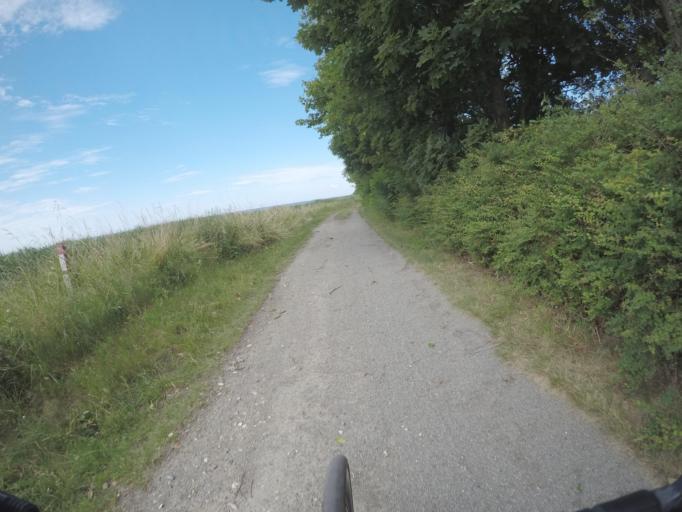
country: DE
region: Mecklenburg-Vorpommern
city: Altefahr
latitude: 54.3617
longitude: 13.1230
